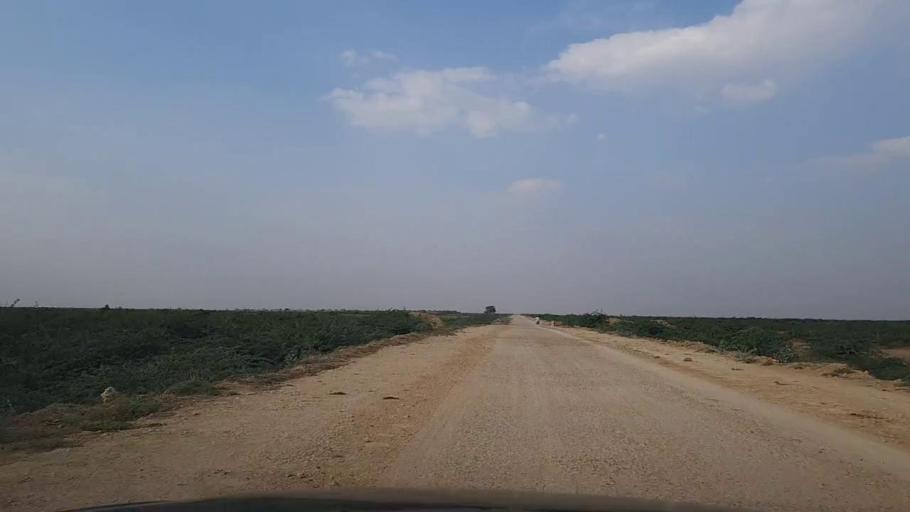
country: PK
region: Sindh
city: Gharo
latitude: 24.8248
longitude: 67.7450
